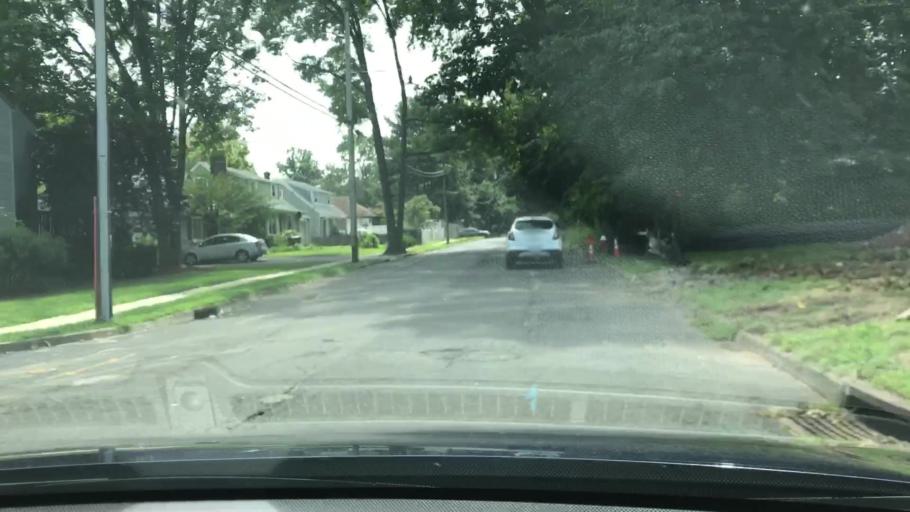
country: US
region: New Jersey
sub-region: Bergen County
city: Bergenfield
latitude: 40.9184
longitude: -74.0050
